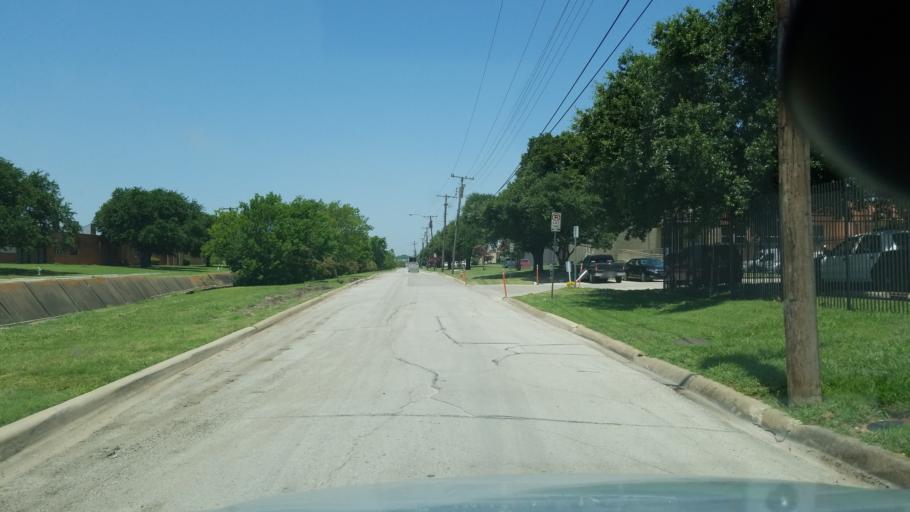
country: US
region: Texas
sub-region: Dallas County
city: Irving
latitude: 32.8145
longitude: -96.8805
